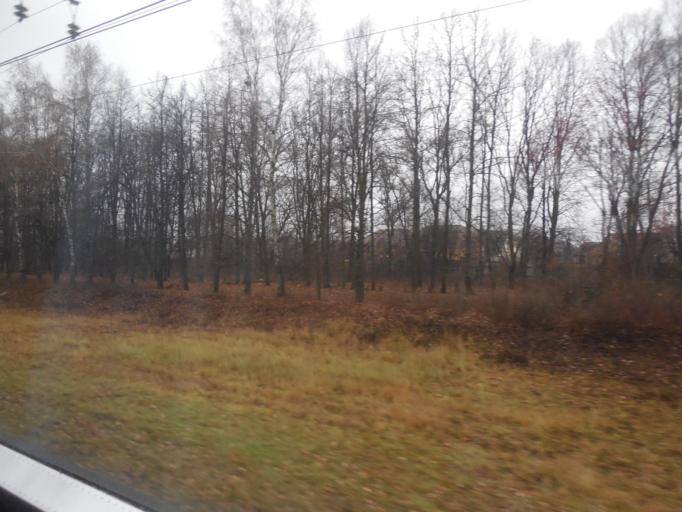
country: RU
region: Moscow
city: Zagor'ye
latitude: 55.5593
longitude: 37.6730
